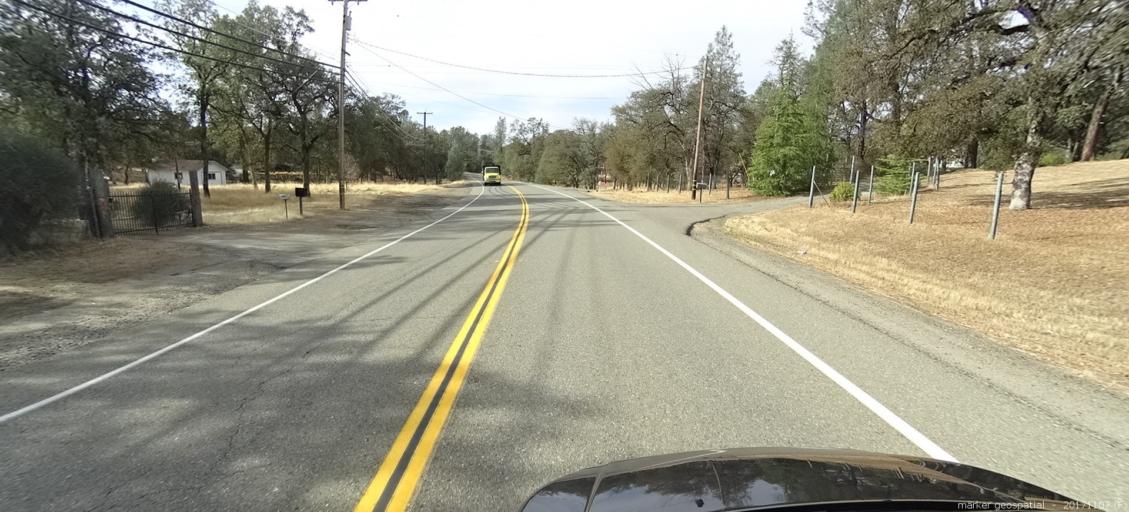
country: US
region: California
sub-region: Shasta County
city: Redding
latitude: 40.5550
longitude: -122.4420
